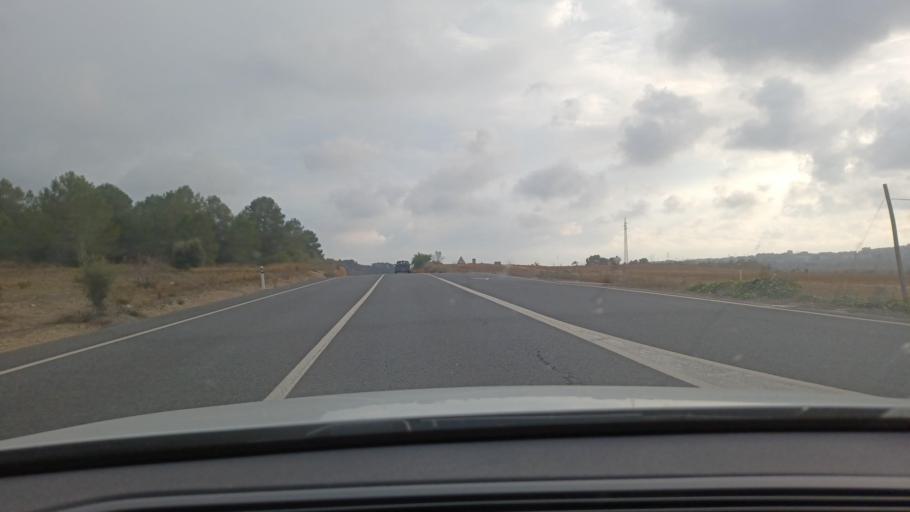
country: ES
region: Catalonia
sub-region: Provincia de Tarragona
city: la Pobla de Mafumet
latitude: 41.1733
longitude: 1.2398
